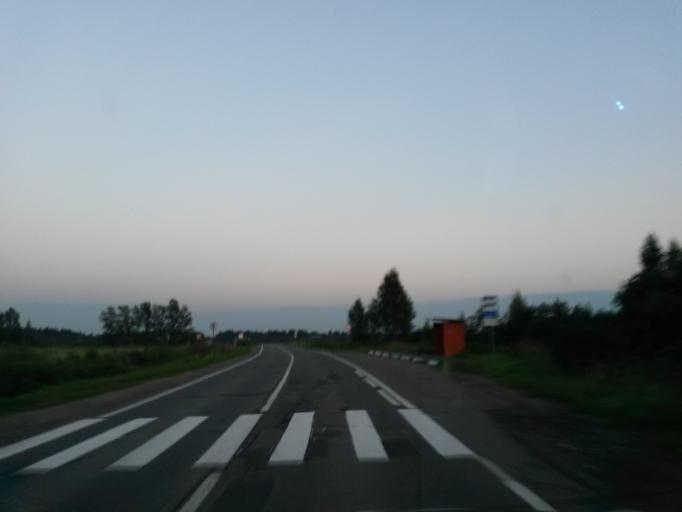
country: RU
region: Jaroslavl
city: Yaroslavl
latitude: 57.7915
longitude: 39.8302
